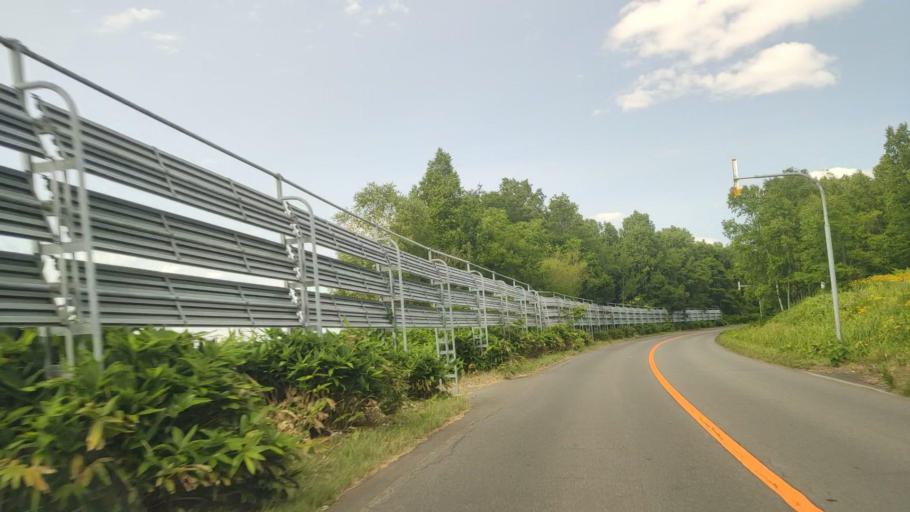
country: JP
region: Hokkaido
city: Nayoro
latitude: 44.2485
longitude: 142.4157
